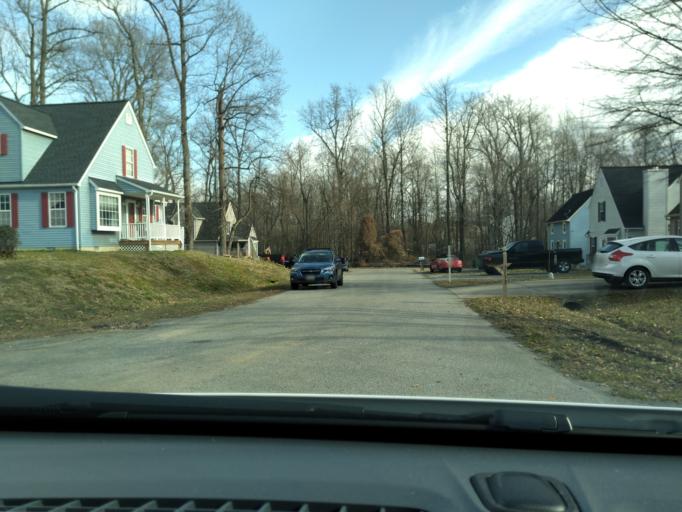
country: US
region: Maryland
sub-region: Calvert County
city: North Beach
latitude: 38.7119
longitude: -76.5406
